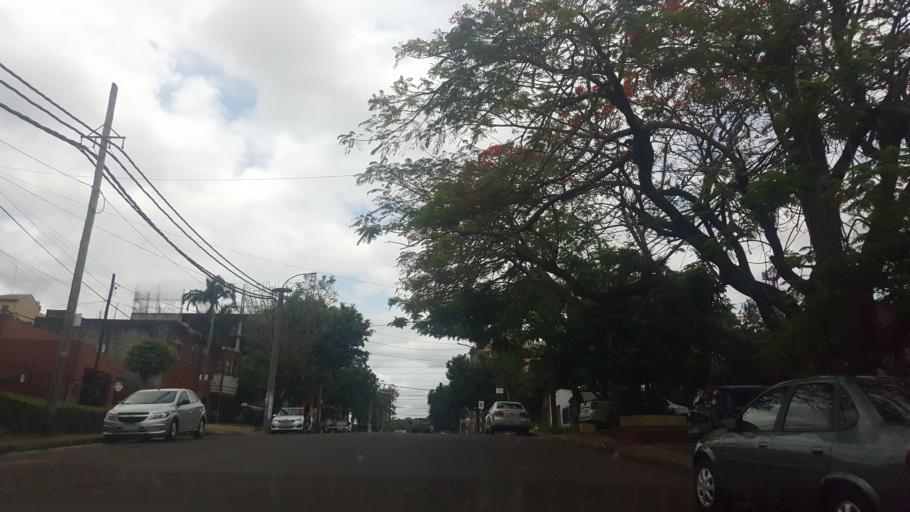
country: AR
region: Misiones
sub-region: Departamento de Capital
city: Posadas
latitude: -27.3663
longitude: -55.9099
